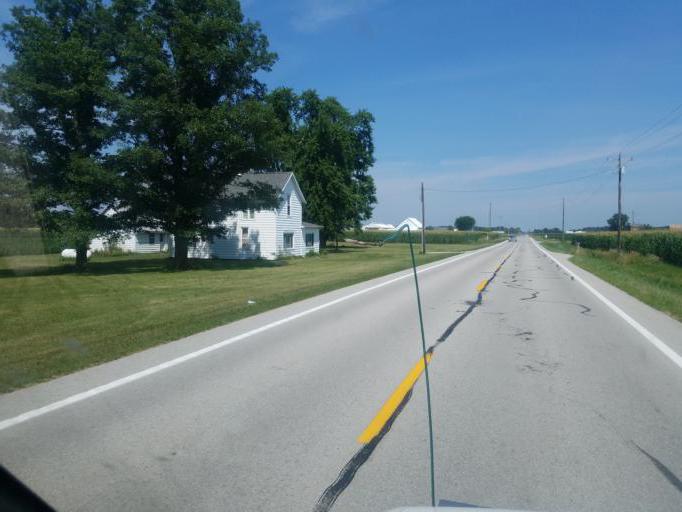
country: US
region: Ohio
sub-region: Auglaize County
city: Saint Marys
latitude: 40.4952
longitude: -84.3693
